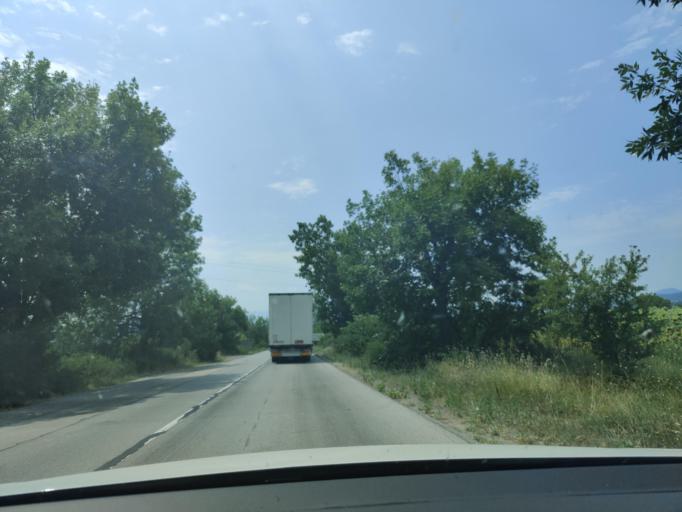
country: BG
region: Vidin
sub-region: Obshtina Ruzhintsi
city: Ruzhintsi
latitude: 43.6243
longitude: 22.8202
